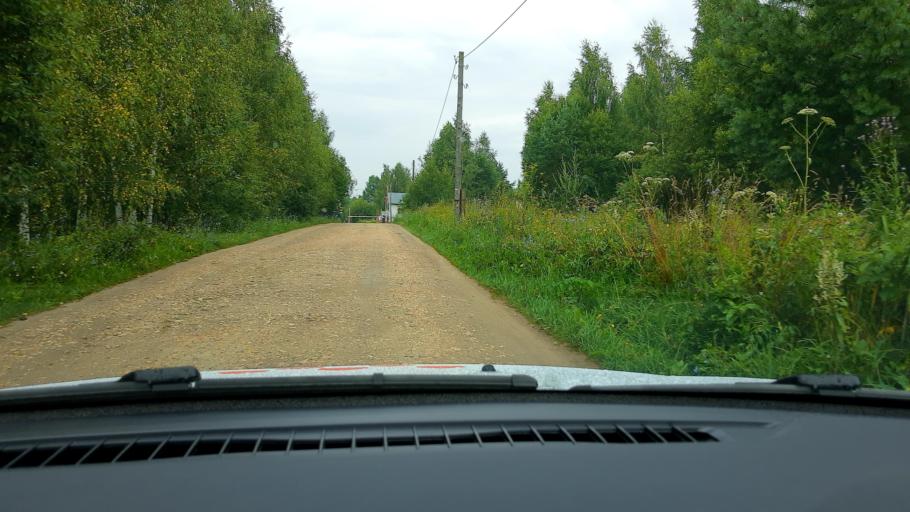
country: RU
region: Nizjnij Novgorod
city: Surovatikha
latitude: 55.9312
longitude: 43.9213
